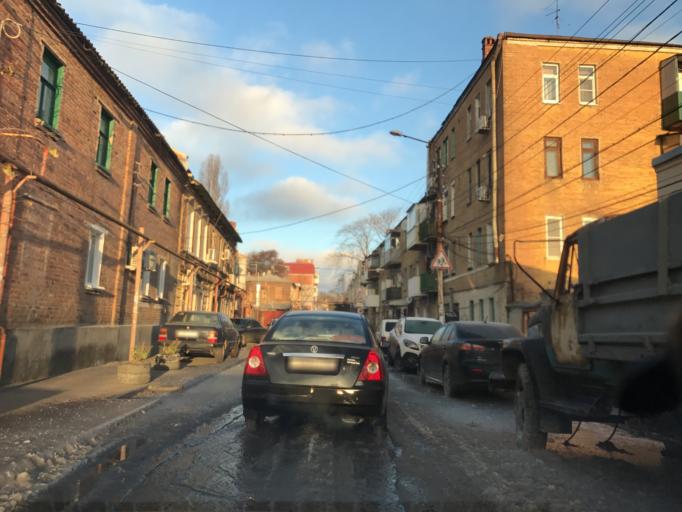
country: RU
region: Rostov
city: Rostov-na-Donu
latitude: 47.2167
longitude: 39.6870
